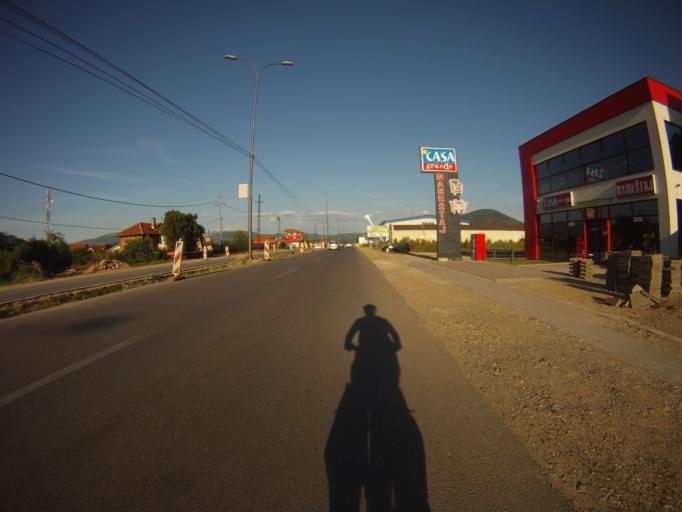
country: RS
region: Central Serbia
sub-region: Nisavski Okrug
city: Niska Banja
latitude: 43.3058
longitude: 21.9628
